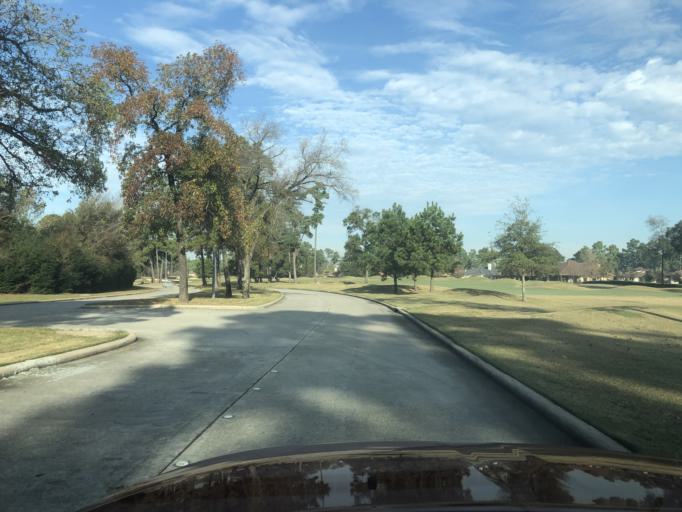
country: US
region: Texas
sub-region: Harris County
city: Spring
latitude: 30.0032
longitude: -95.4729
